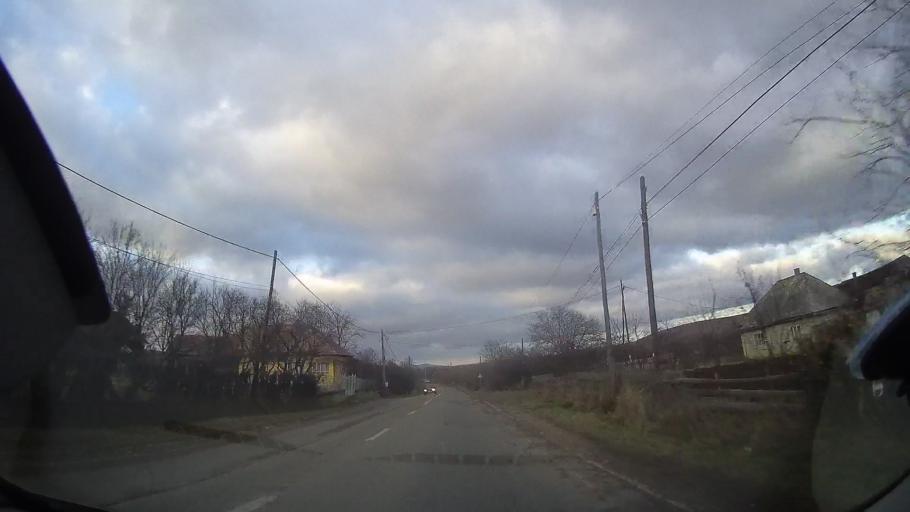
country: RO
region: Cluj
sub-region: Comuna Sancraiu
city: Sancraiu
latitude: 46.8052
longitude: 22.9945
